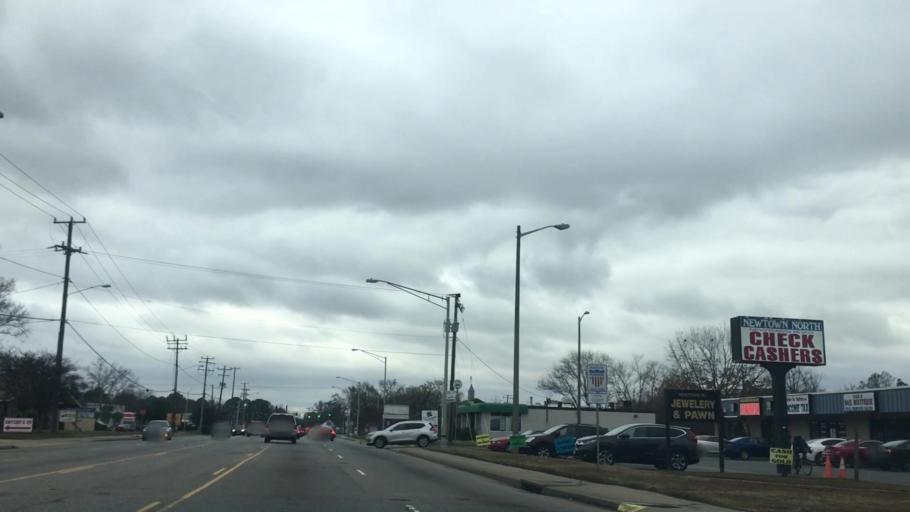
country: US
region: Virginia
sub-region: City of Chesapeake
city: Chesapeake
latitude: 36.8567
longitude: -76.1771
